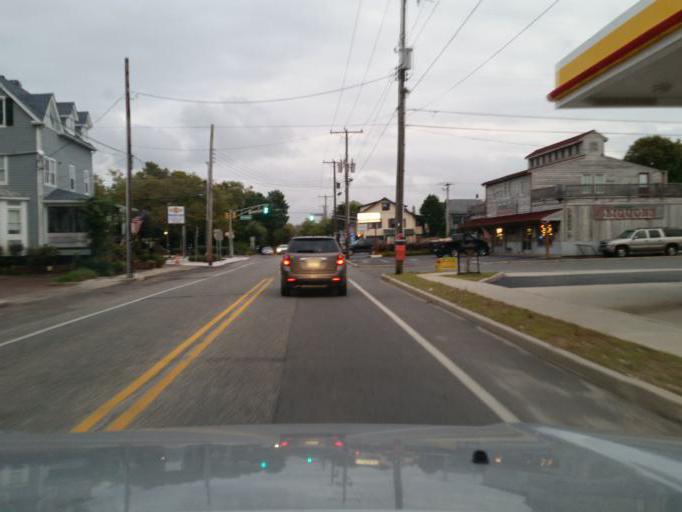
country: US
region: New Jersey
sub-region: Cape May County
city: West Cape May
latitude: 38.9353
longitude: -74.9318
